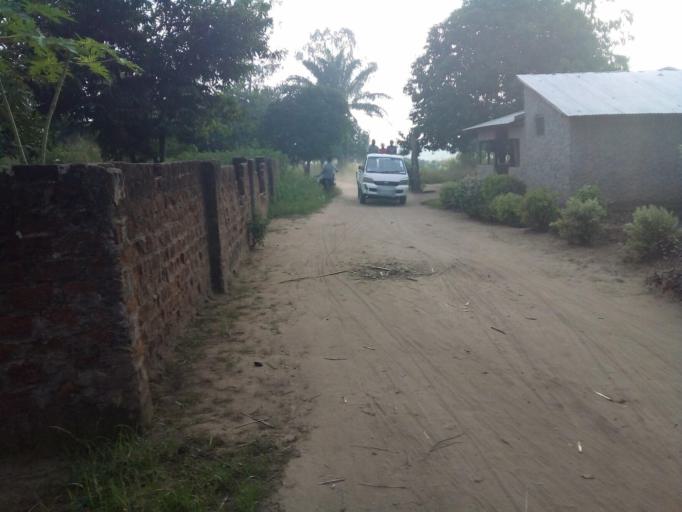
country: MZ
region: Zambezia
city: Quelimane
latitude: -17.5845
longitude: 36.6891
